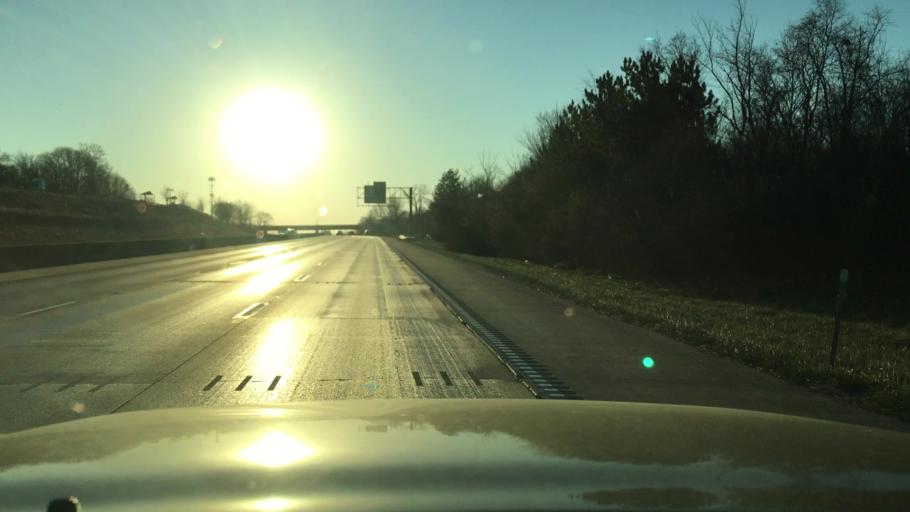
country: US
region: Missouri
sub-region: Saint Charles County
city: Saint Charles
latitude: 38.8097
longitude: -90.4859
